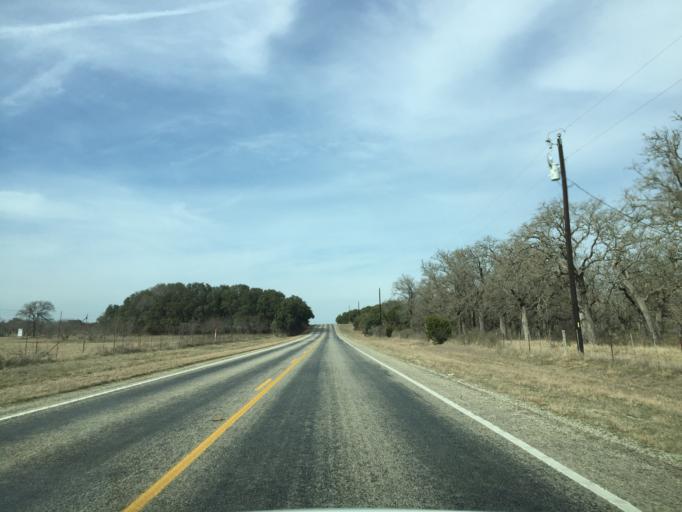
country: US
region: Texas
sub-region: Gillespie County
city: Fredericksburg
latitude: 30.4246
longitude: -98.7370
